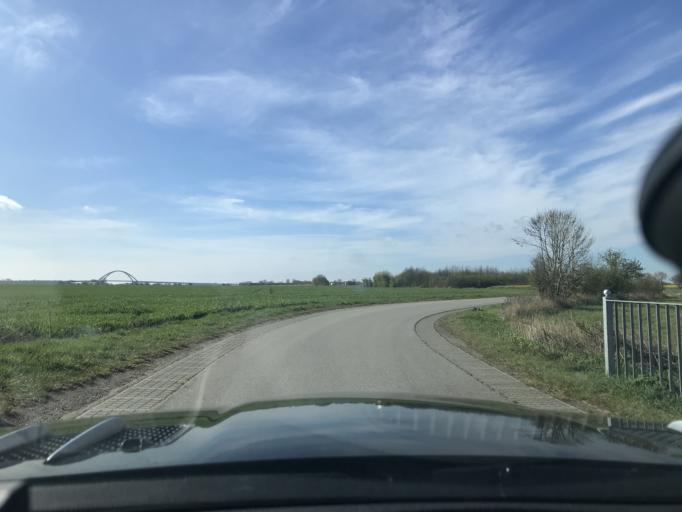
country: DE
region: Schleswig-Holstein
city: Grossenbrode
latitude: 54.4244
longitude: 11.1037
